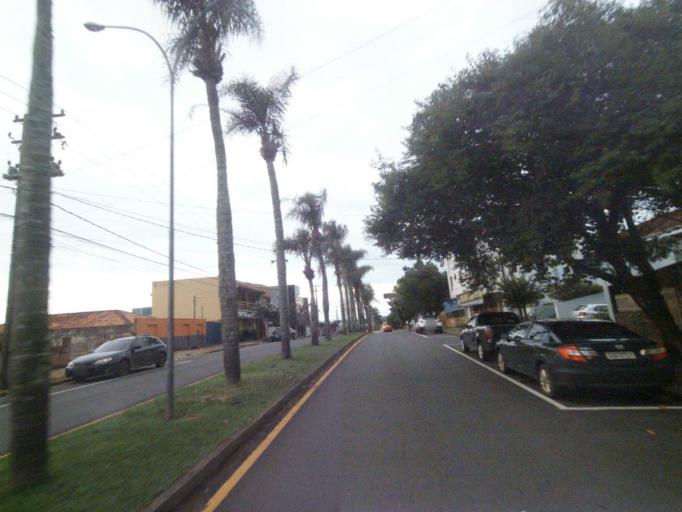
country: BR
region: Parana
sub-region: Telemaco Borba
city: Telemaco Borba
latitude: -24.3295
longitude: -50.6238
